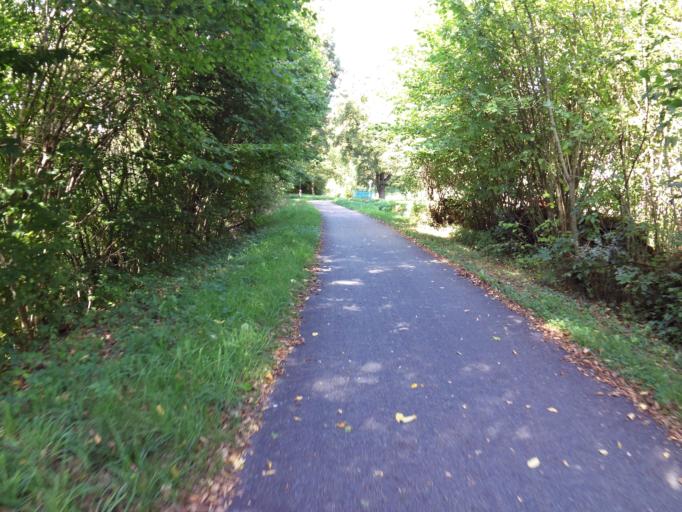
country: DE
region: Rheinland-Pfalz
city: Irrel
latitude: 49.8448
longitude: 6.4712
